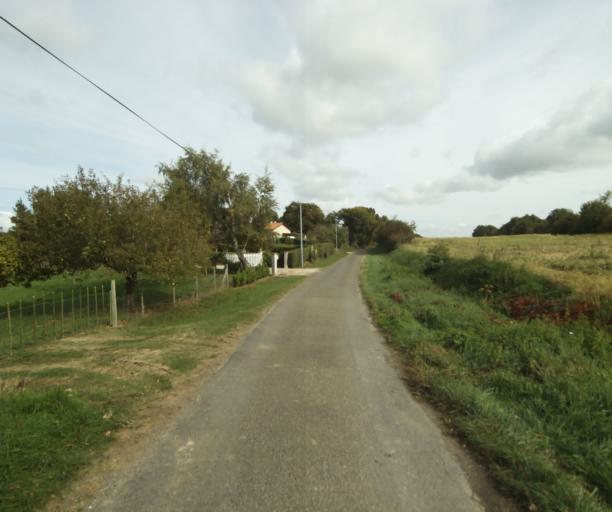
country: FR
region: Midi-Pyrenees
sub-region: Departement du Gers
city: Eauze
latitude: 43.8321
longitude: 0.1234
